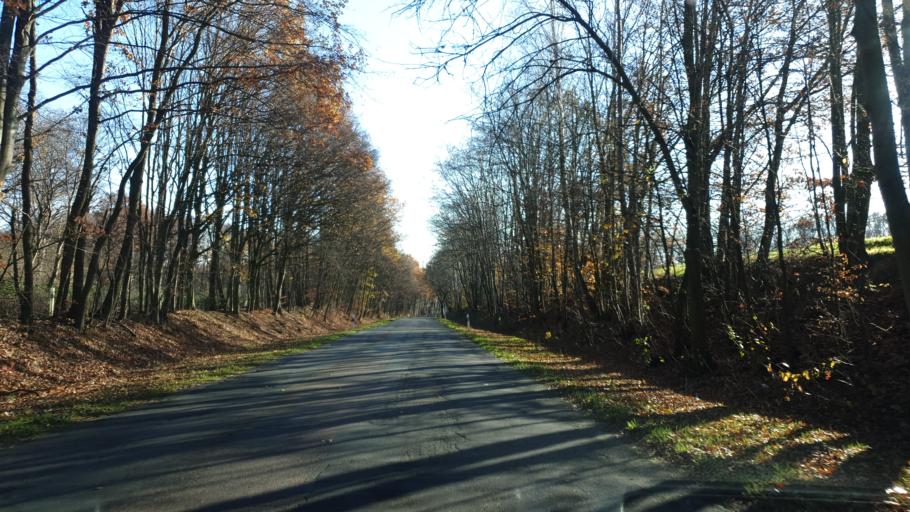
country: DE
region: Saxony-Anhalt
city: Wetterzeube
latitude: 51.0135
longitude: 12.0028
